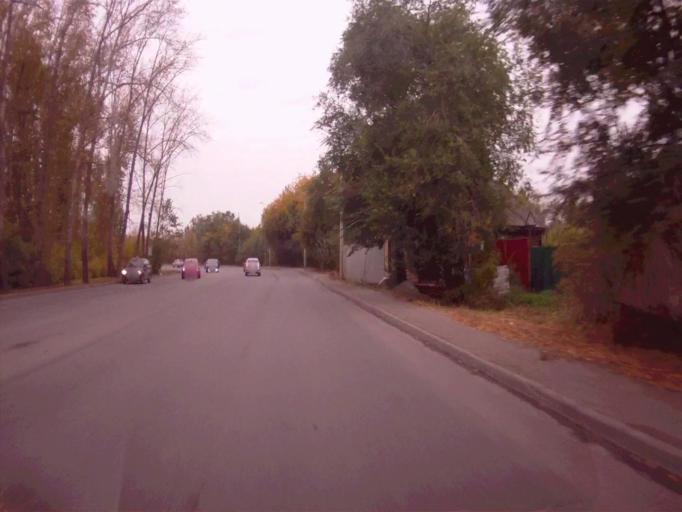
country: RU
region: Chelyabinsk
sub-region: Gorod Chelyabinsk
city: Chelyabinsk
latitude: 55.1341
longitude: 61.3864
